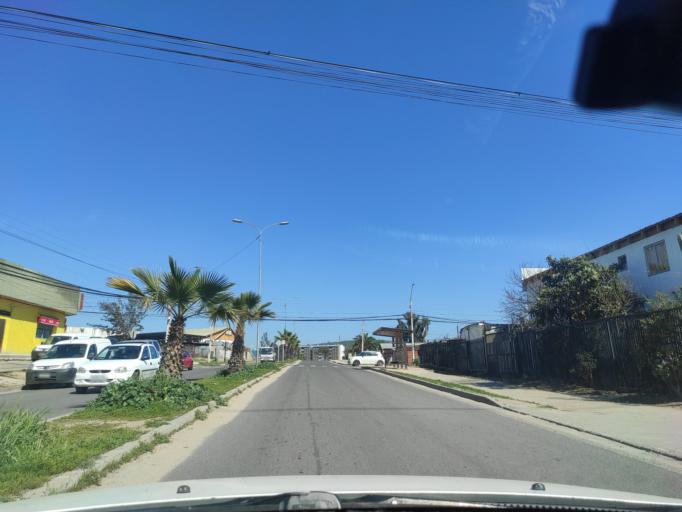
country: CL
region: Valparaiso
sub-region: Provincia de Marga Marga
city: Limache
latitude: -33.0154
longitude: -71.2569
